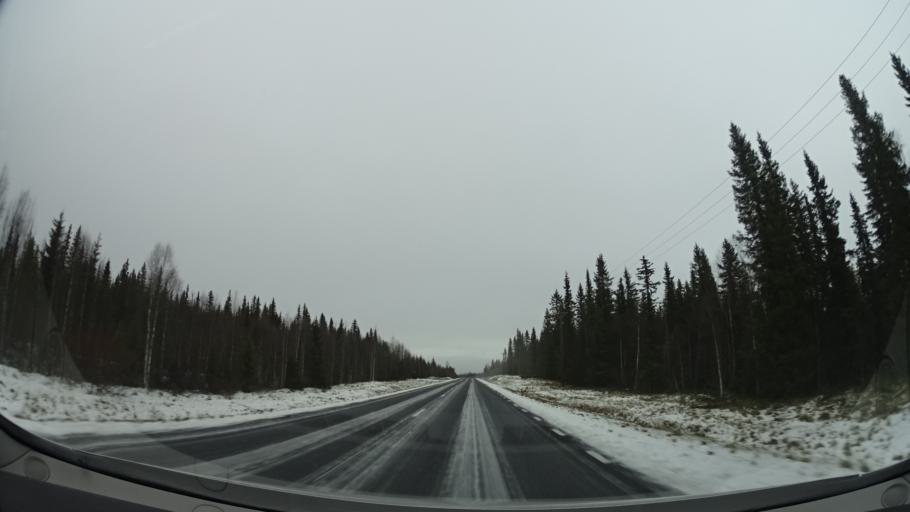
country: SE
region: Vaesterbotten
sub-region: Lycksele Kommun
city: Soderfors
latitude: 64.4380
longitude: 18.1094
